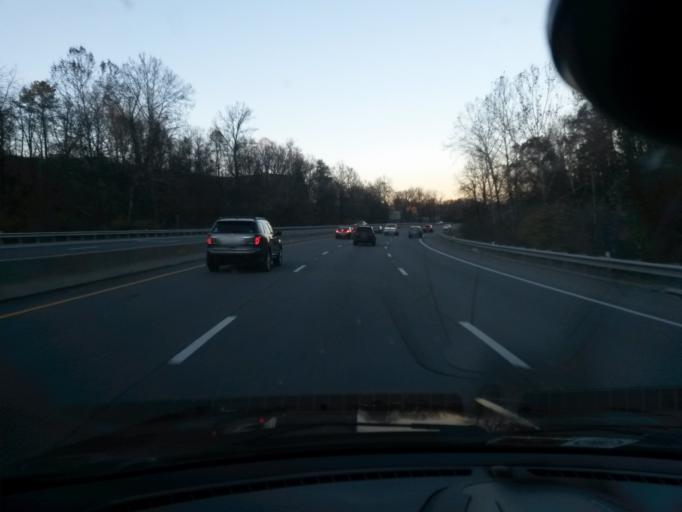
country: US
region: Virginia
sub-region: Roanoke County
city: Narrows
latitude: 37.2427
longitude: -79.9716
